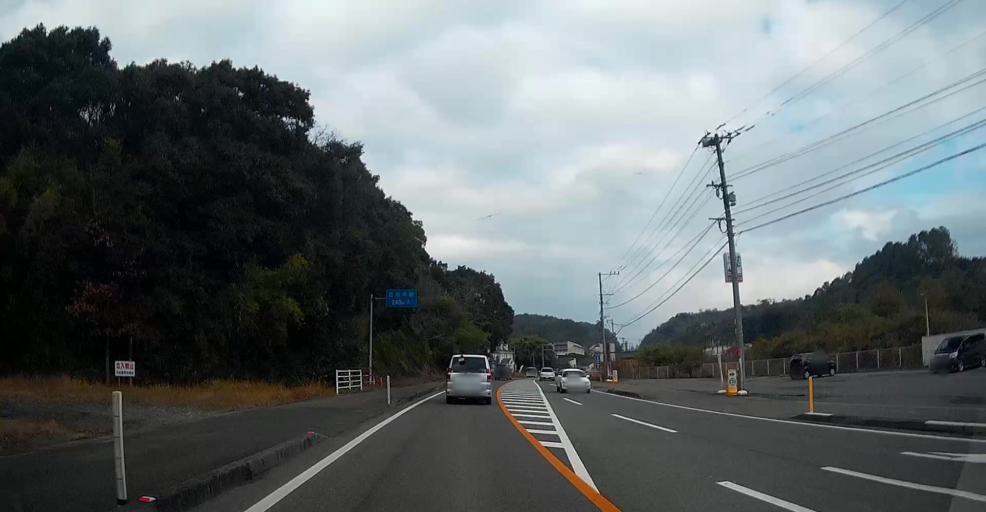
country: JP
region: Kumamoto
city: Yatsushiro
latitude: 32.5529
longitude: 130.4175
